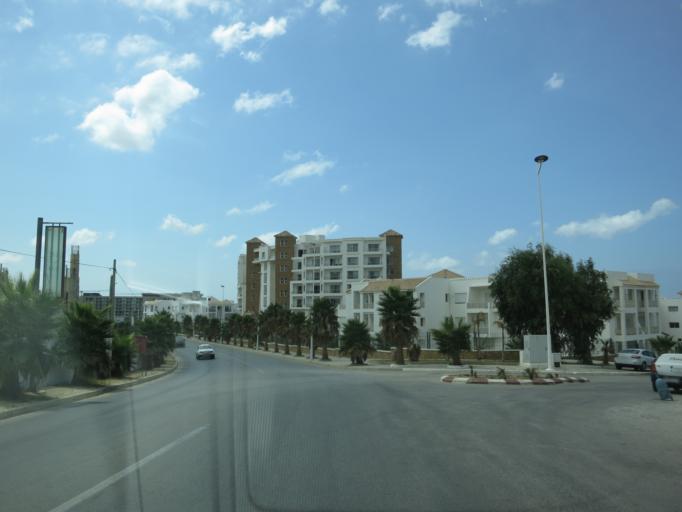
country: MA
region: Tanger-Tetouan
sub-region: Tanger-Assilah
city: Tangier
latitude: 35.7873
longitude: -5.7589
